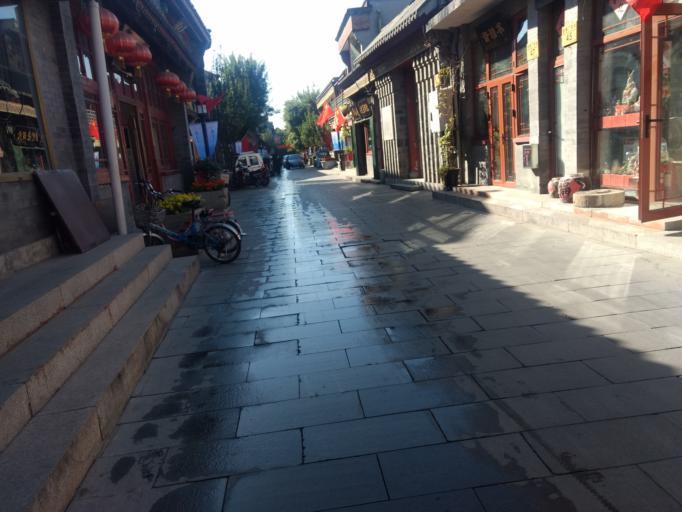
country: CN
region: Beijing
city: Beijing
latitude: 39.8938
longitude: 116.3816
